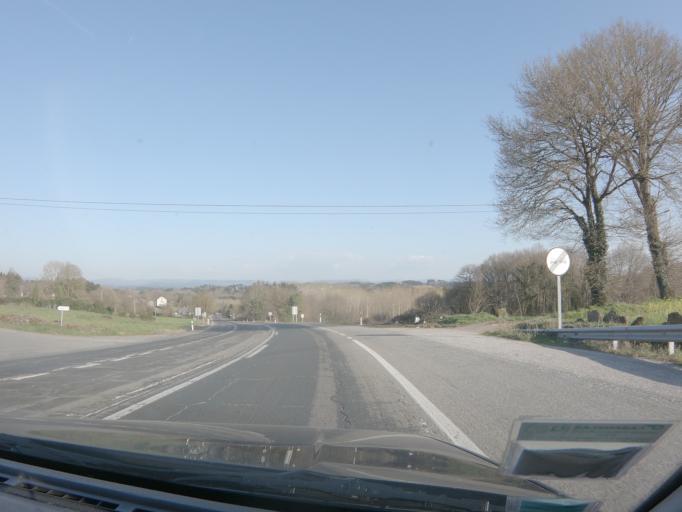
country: ES
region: Galicia
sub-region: Provincia de Lugo
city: Corgo
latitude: 42.9646
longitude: -7.4930
